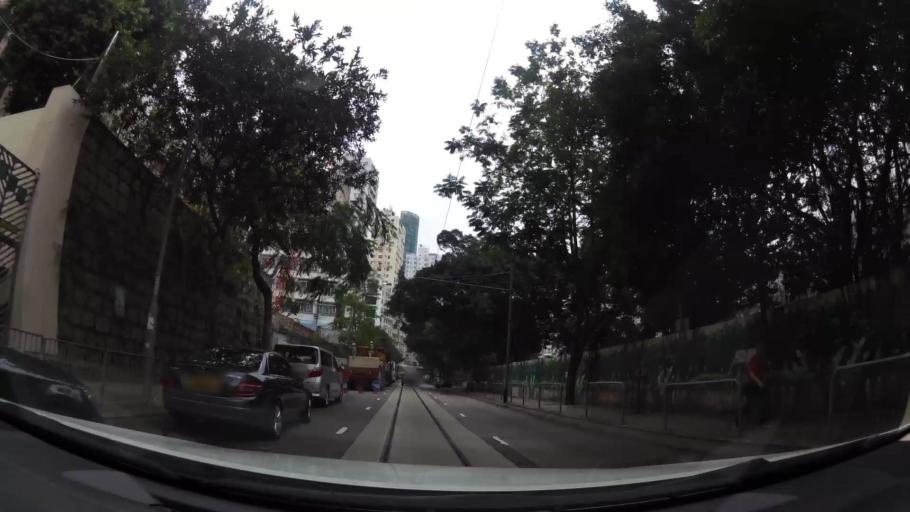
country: HK
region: Wanchai
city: Wan Chai
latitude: 22.2730
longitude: 114.1841
